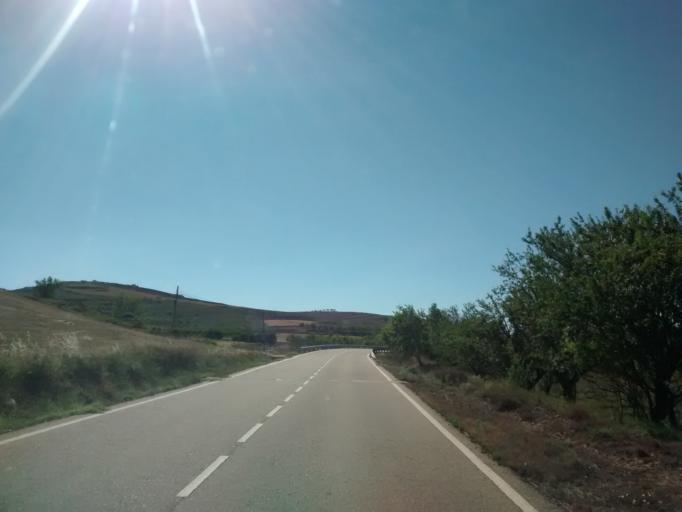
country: ES
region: Aragon
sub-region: Provincia de Zaragoza
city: Trasmoz
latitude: 41.8390
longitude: -1.7128
